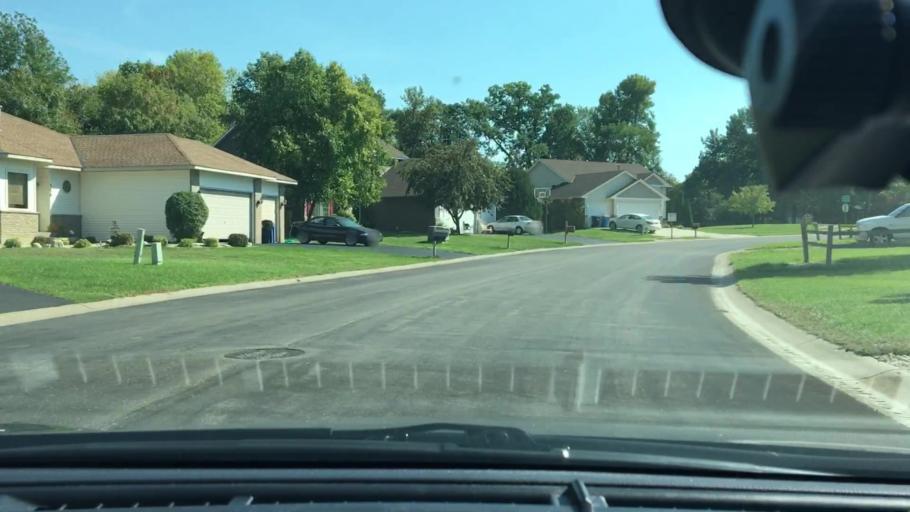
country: US
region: Minnesota
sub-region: Wright County
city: Saint Michael
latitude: 45.2046
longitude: -93.6764
